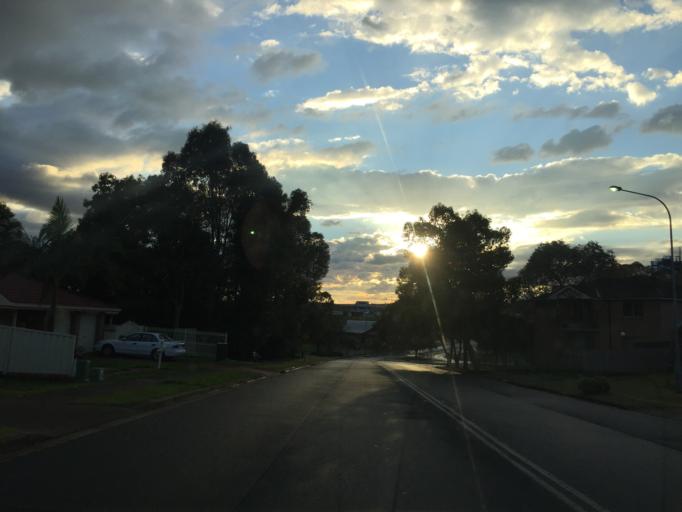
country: AU
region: New South Wales
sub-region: Shellharbour
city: Barrack Heights
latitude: -34.5661
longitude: 150.8321
